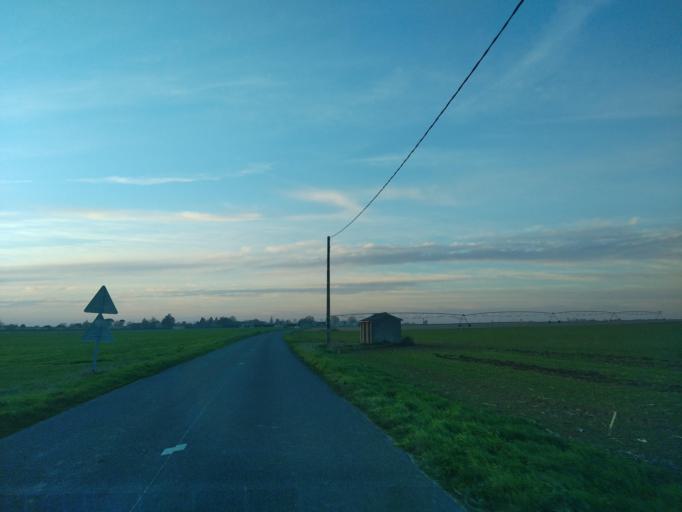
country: FR
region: Pays de la Loire
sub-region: Departement de la Vendee
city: Vix
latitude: 46.3972
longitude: -0.8341
